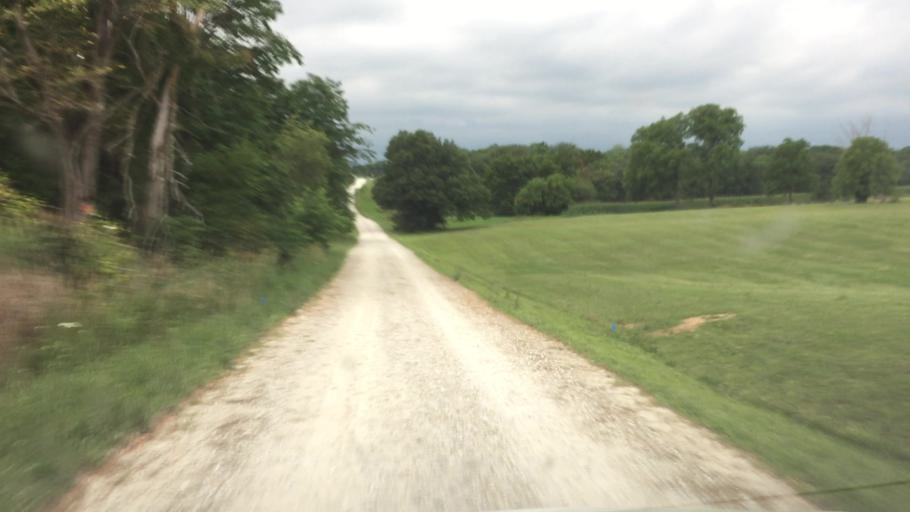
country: US
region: Illinois
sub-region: Adams County
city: Camp Point
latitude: 40.2156
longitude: -90.9517
